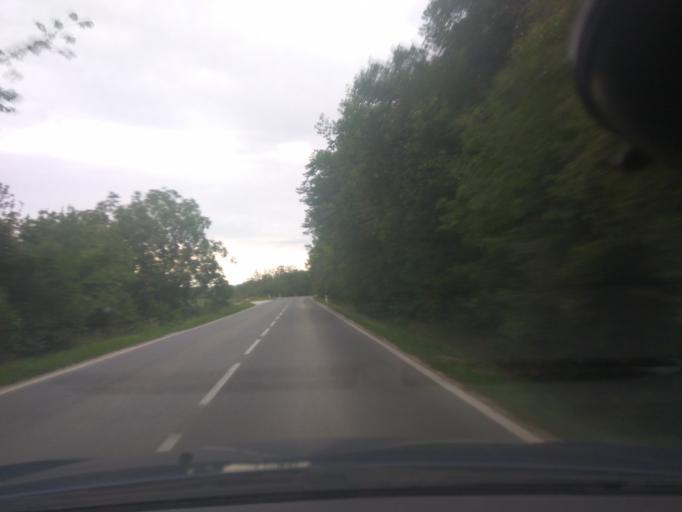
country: SK
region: Trnavsky
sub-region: Okres Trnava
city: Piestany
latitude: 48.6365
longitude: 17.8648
